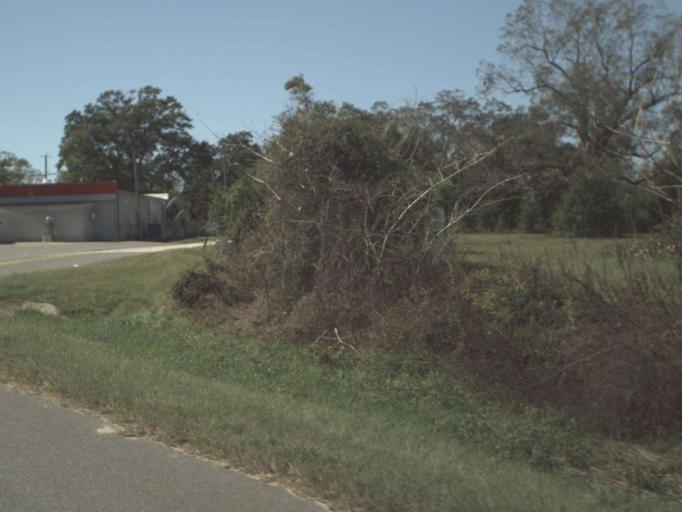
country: US
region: Alabama
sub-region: Covington County
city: Florala
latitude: 30.9672
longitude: -86.4589
